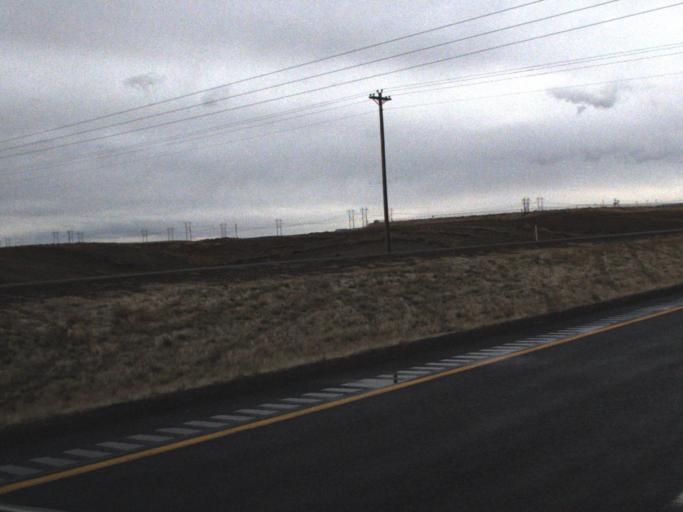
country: US
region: Washington
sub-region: Walla Walla County
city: College Place
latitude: 46.0728
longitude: -118.3885
